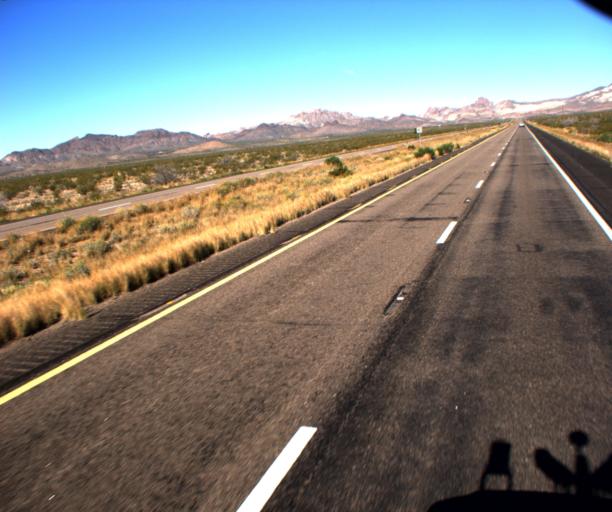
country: US
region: Arizona
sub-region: Mohave County
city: Golden Valley
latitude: 35.2270
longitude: -114.3167
